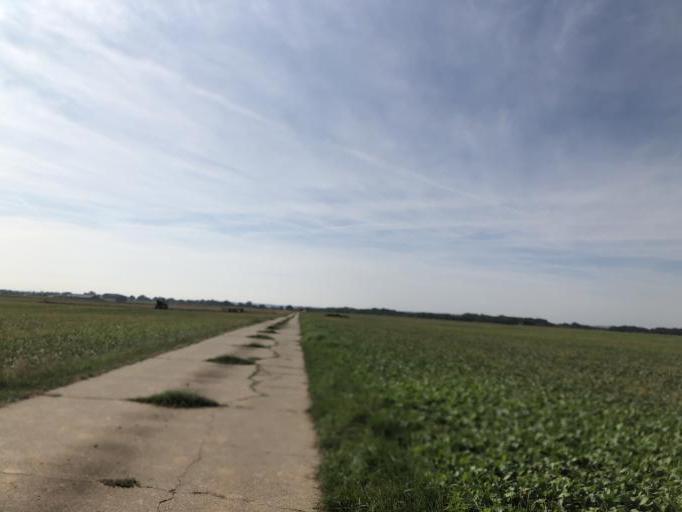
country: DE
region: Bavaria
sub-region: Regierungsbezirk Mittelfranken
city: Obermichelbach
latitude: 49.5403
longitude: 10.9490
